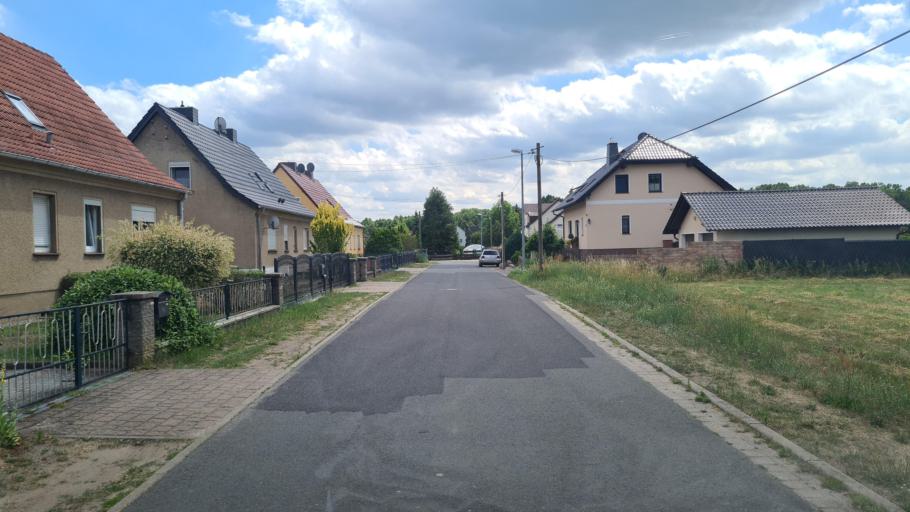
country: DE
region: Brandenburg
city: Luckenwalde
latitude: 52.1115
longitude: 13.2032
